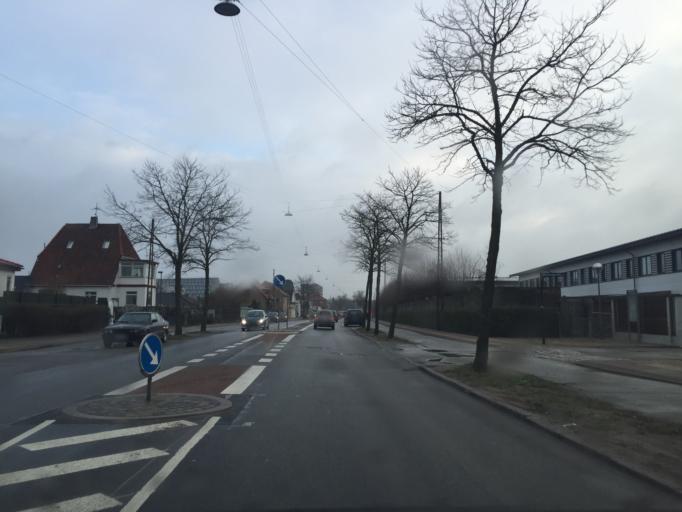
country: DK
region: Capital Region
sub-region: Tarnby Kommune
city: Tarnby
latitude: 55.6496
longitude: 12.5923
